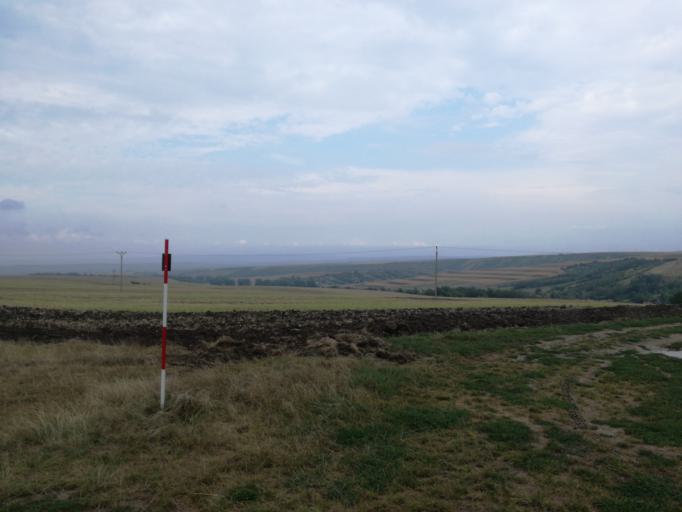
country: CZ
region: South Moravian
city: Bosovice
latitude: 49.0539
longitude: 16.8275
